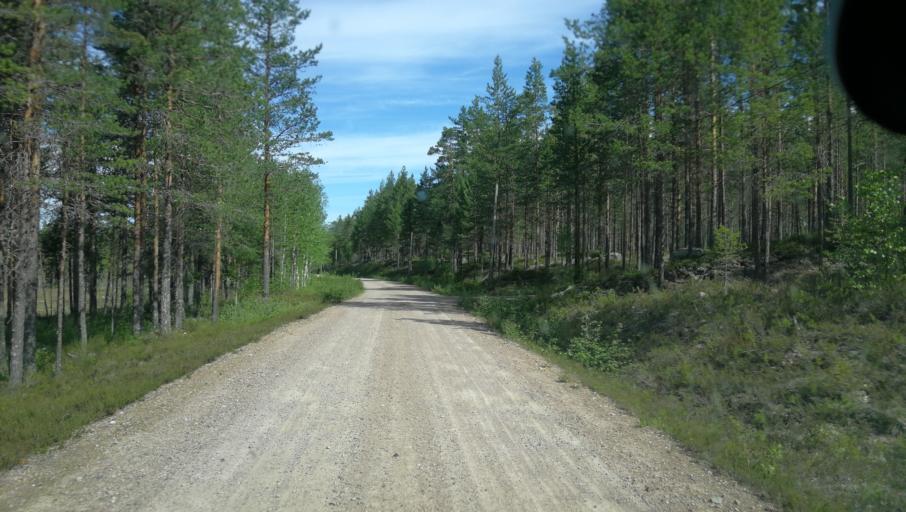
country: SE
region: Dalarna
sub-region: Vansbro Kommun
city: Vansbro
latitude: 60.8370
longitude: 14.1505
